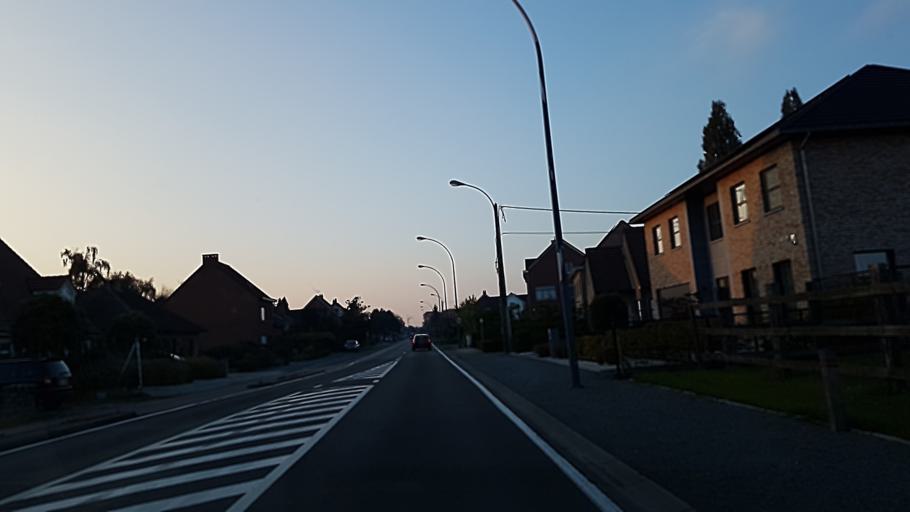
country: BE
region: Flanders
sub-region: Provincie Antwerpen
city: Kontich
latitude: 51.1255
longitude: 4.4589
